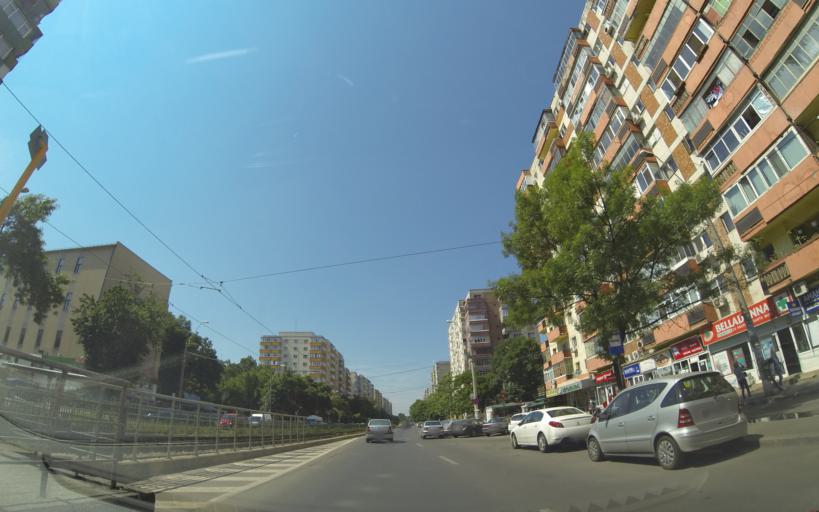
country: RO
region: Bucuresti
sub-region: Municipiul Bucuresti
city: Bucuresti
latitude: 44.4102
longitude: 26.0694
